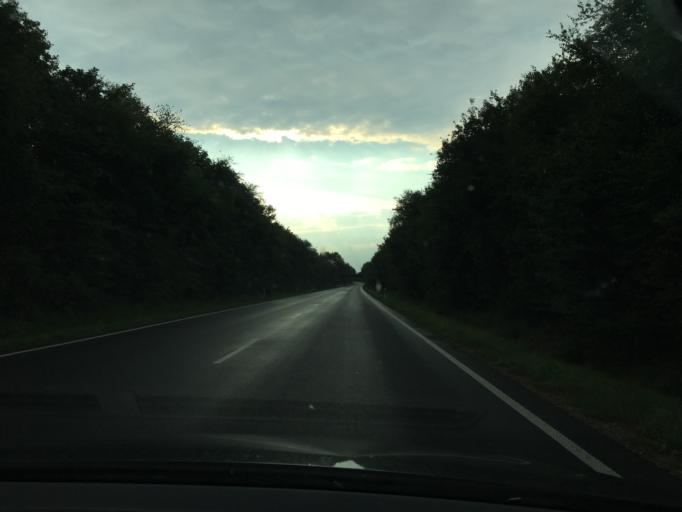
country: DE
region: North Rhine-Westphalia
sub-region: Regierungsbezirk Koln
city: Kerpen
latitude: 50.8235
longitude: 6.7011
